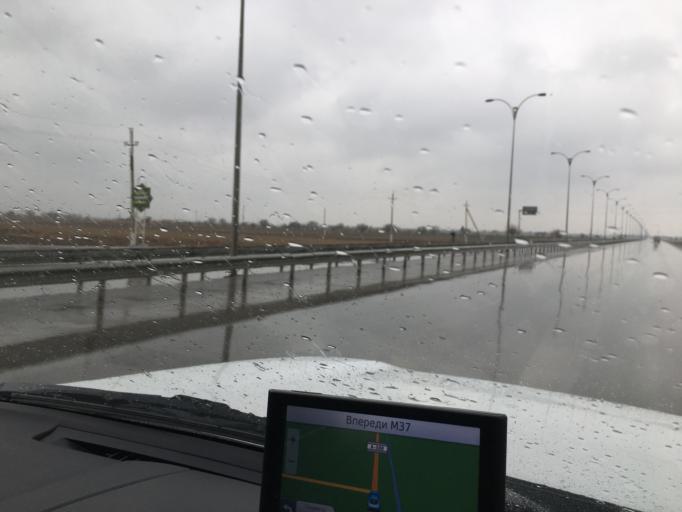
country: TM
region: Mary
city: Mary
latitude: 37.5570
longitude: 61.8544
